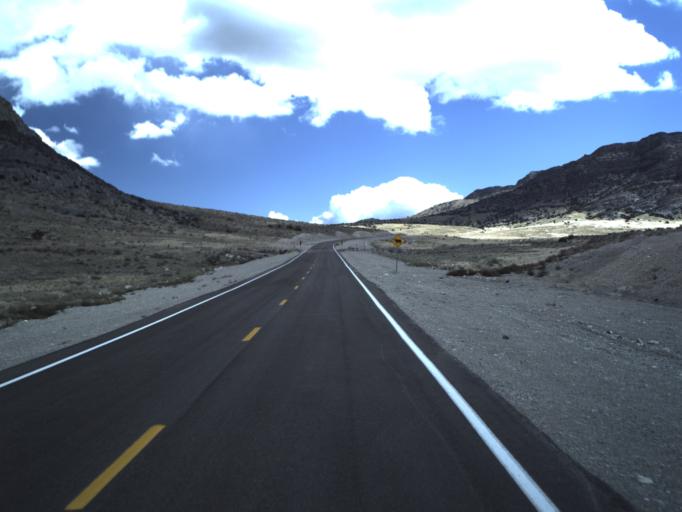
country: US
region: Utah
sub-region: Beaver County
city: Milford
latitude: 38.5058
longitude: -113.6054
